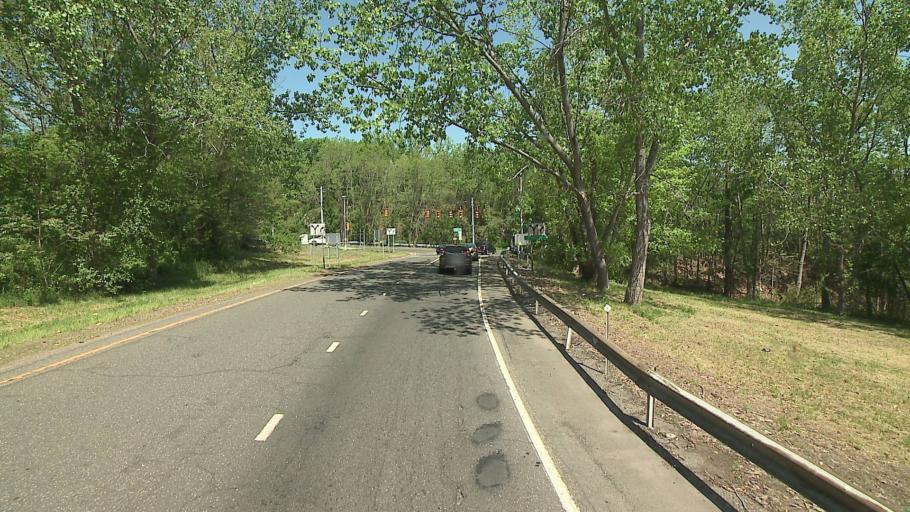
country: US
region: Connecticut
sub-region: New Haven County
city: Waterbury
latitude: 41.5440
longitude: -73.0279
